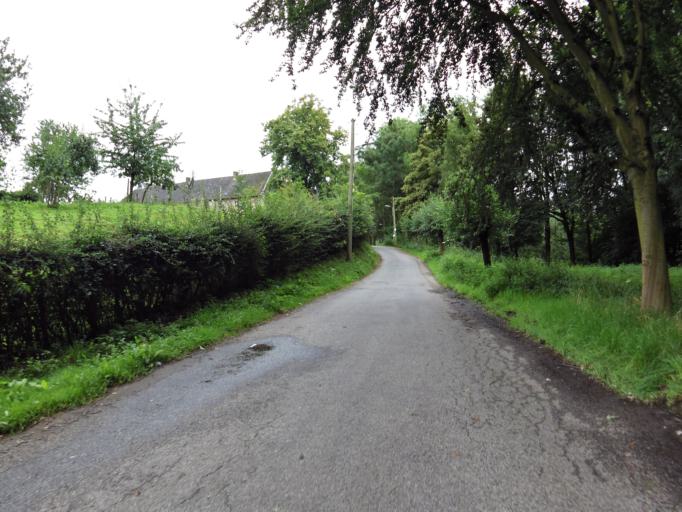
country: NL
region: Limburg
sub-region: Gemeente Heerlen
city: Heerlen
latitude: 50.8752
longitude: 5.9986
